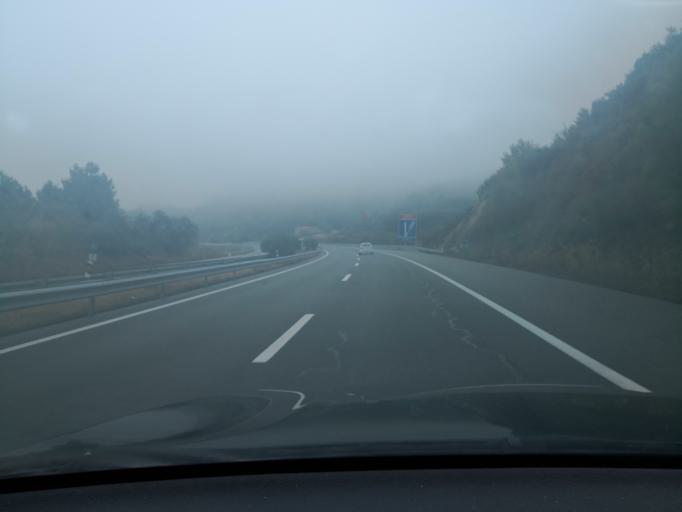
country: PT
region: Braga
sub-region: Celorico de Basto
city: Celorico de Basto
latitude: 41.4472
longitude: -8.0605
